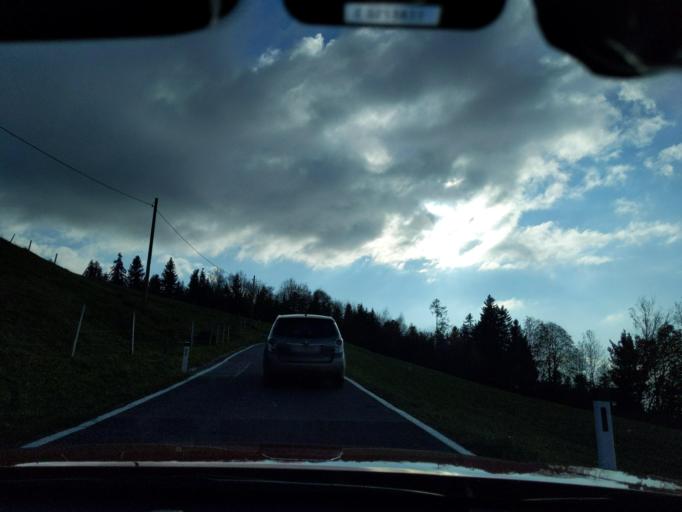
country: AT
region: Vorarlberg
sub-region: Politischer Bezirk Bregenz
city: Hohenweiler
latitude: 47.5591
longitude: 9.7892
